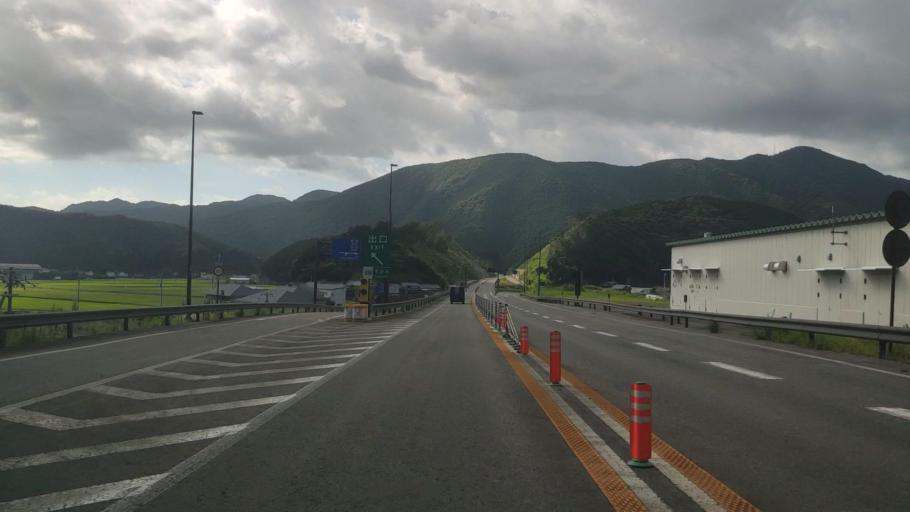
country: JP
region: Wakayama
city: Tanabe
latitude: 33.5541
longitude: 135.5110
